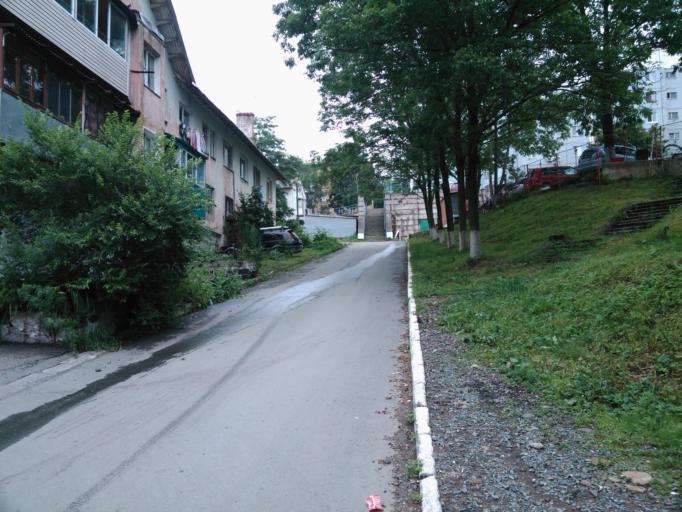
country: RU
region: Primorskiy
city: Vladivostok
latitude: 43.0945
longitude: 131.9571
